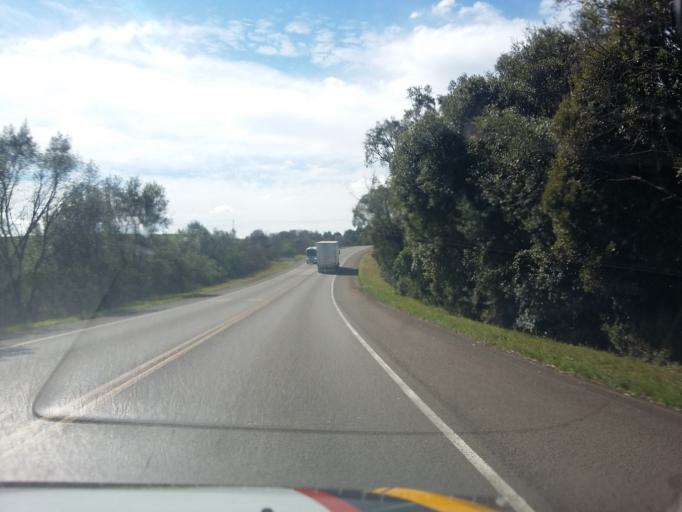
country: BR
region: Rio Grande do Sul
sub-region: Vacaria
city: Vacaria
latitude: -28.6078
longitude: -51.0413
